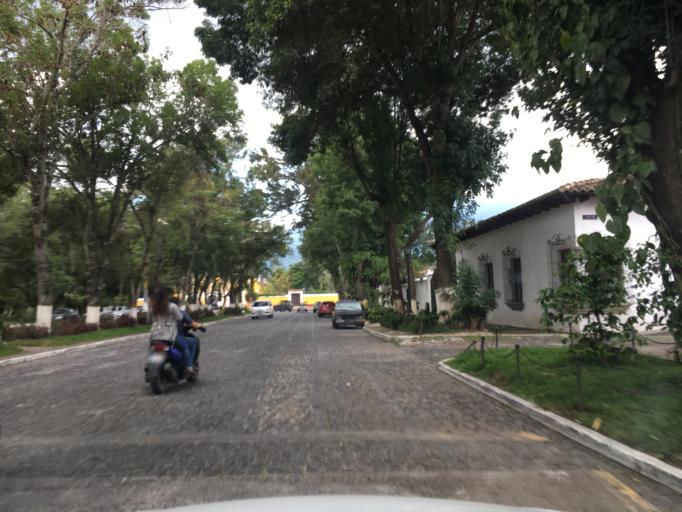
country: GT
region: Sacatepequez
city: Antigua Guatemala
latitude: 14.5466
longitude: -90.7300
